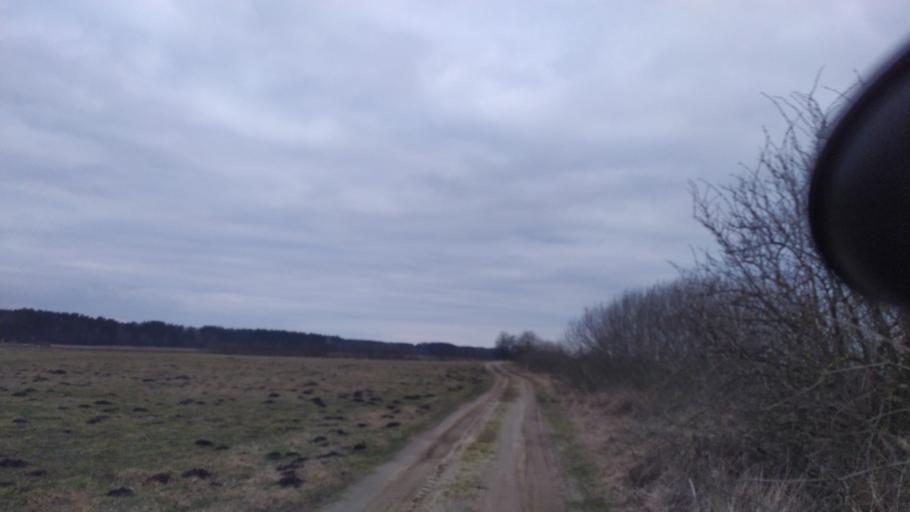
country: PL
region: Lublin Voivodeship
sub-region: Powiat lubartowski
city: Abramow
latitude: 51.4305
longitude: 22.3170
